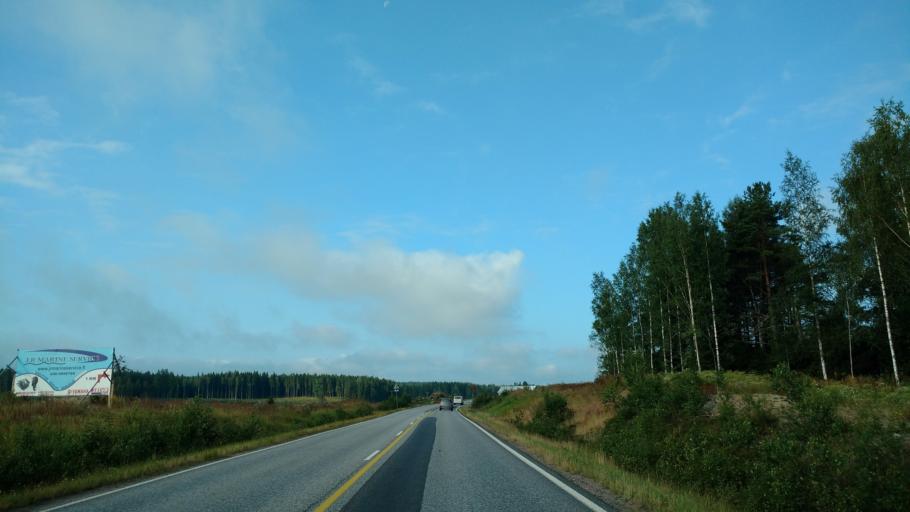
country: FI
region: Varsinais-Suomi
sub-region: Aboland-Turunmaa
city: Vaestanfjaerd
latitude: 60.1053
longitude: 22.5914
